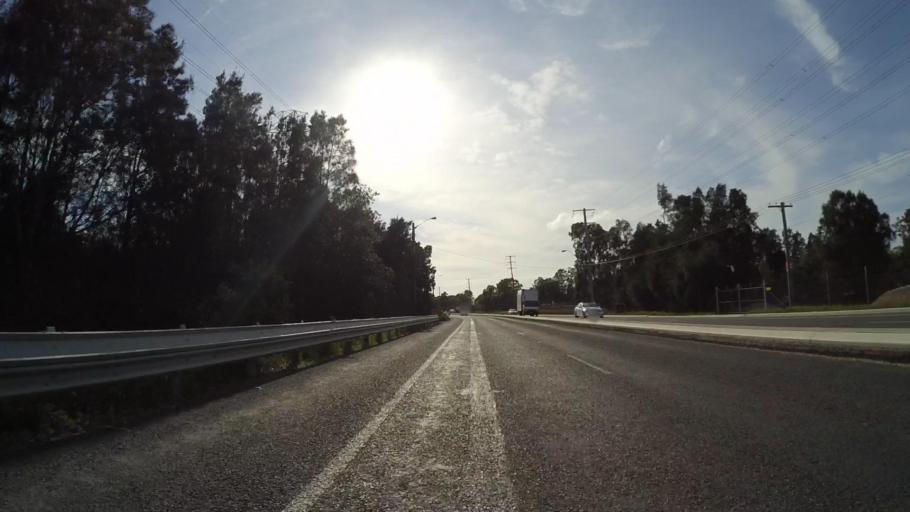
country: AU
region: New South Wales
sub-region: Sutherland Shire
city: Cronulla
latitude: -34.0395
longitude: 151.1530
